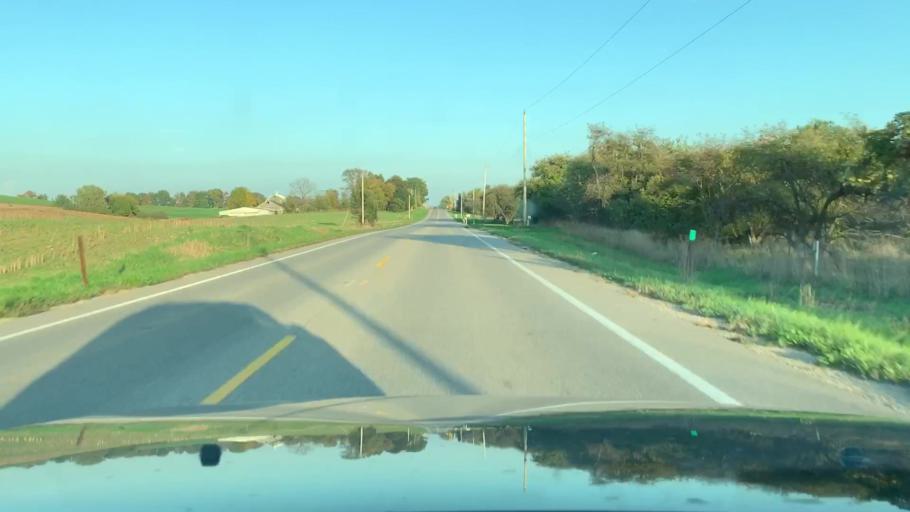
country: US
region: Michigan
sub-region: Ottawa County
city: Hudsonville
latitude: 42.8115
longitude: -85.8097
